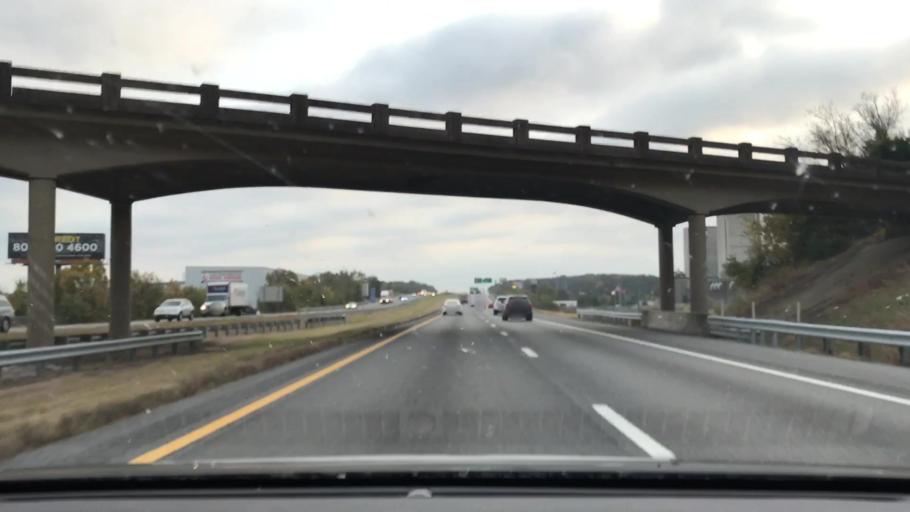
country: US
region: Tennessee
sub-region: Wilson County
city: Lebanon
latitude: 36.1863
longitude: -86.2759
